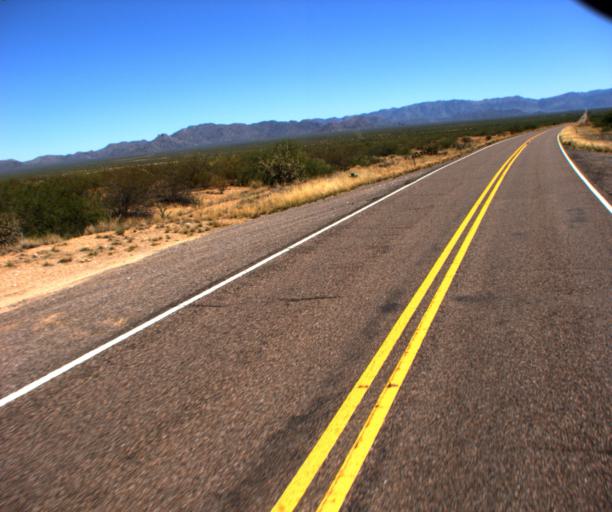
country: US
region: Arizona
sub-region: Yavapai County
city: Congress
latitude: 34.1077
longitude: -112.9899
